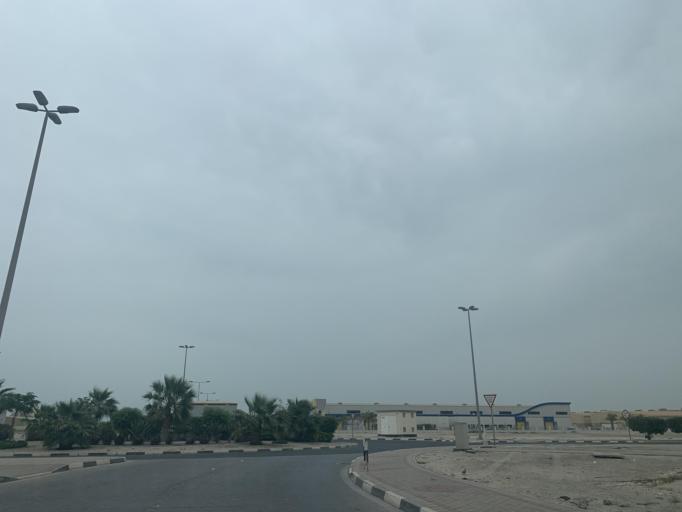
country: BH
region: Muharraq
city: Al Hadd
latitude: 26.2133
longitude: 50.6725
